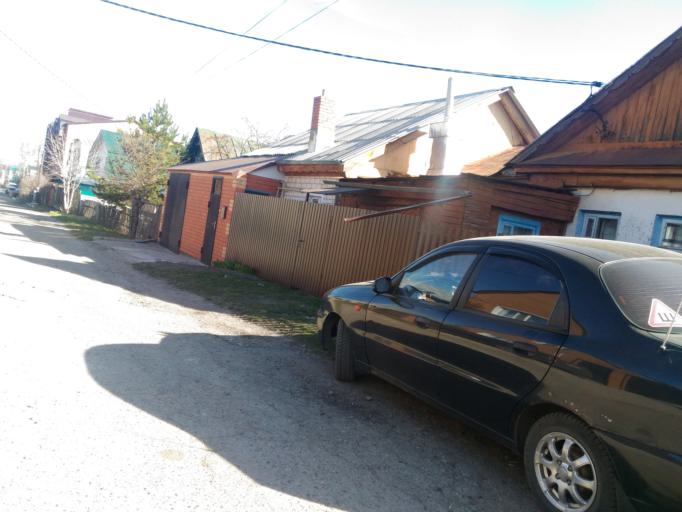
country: RU
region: Ulyanovsk
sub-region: Ulyanovskiy Rayon
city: Ulyanovsk
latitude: 54.3509
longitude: 48.3785
